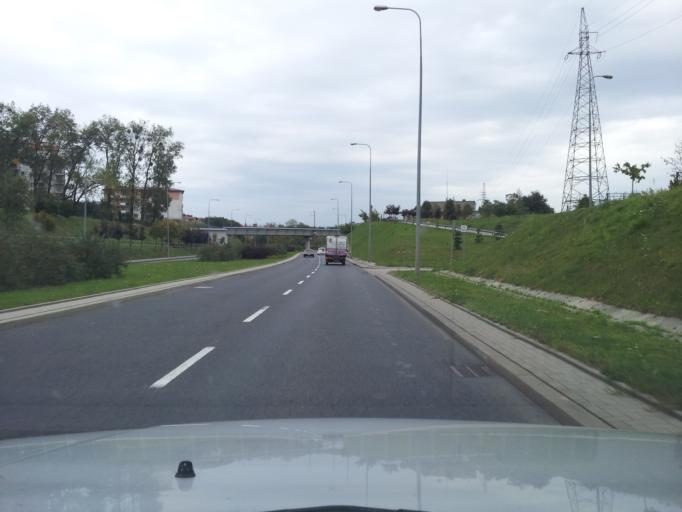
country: PL
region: Warmian-Masurian Voivodeship
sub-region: Olsztyn
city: Kortowo
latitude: 53.7760
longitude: 20.4591
